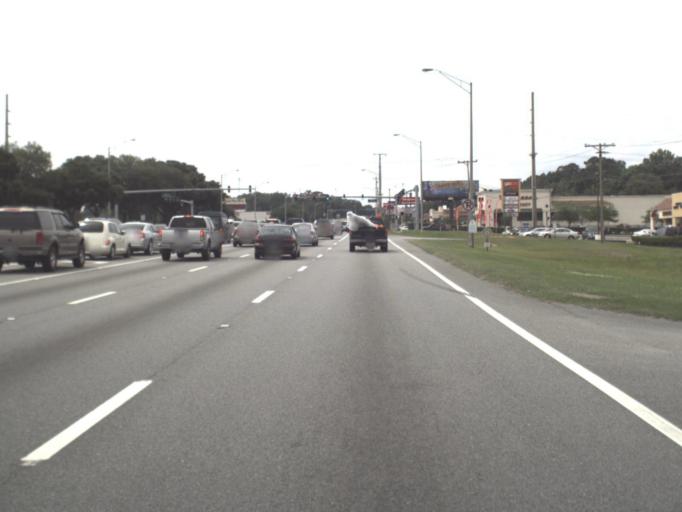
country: US
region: Florida
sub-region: Clay County
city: Bellair-Meadowbrook Terrace
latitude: 30.1886
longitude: -81.7395
